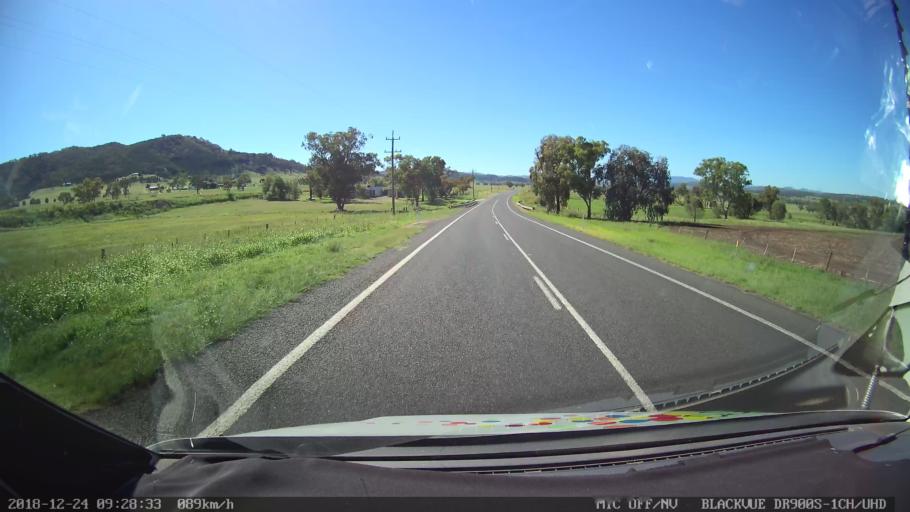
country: AU
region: New South Wales
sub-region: Liverpool Plains
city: Quirindi
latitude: -31.5391
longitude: 150.6897
